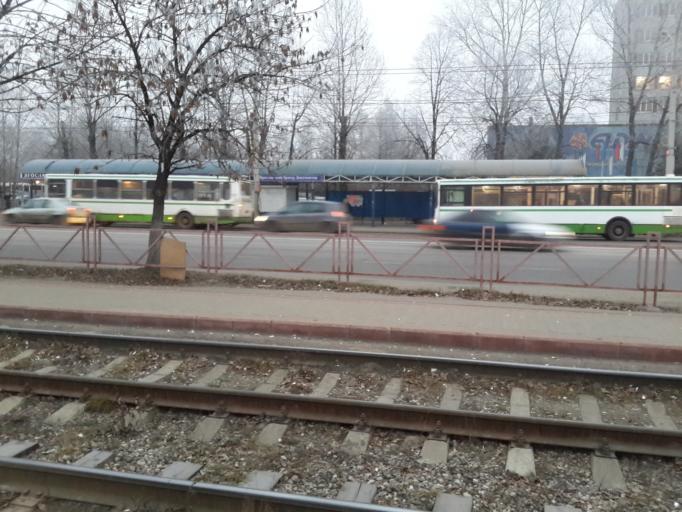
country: RU
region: Jaroslavl
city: Yaroslavl
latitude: 57.6473
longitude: 39.8501
